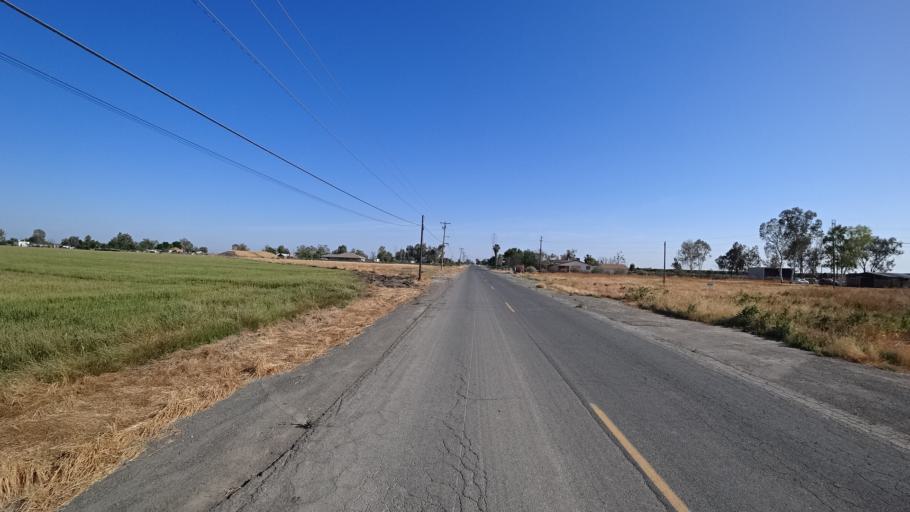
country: US
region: California
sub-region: Kings County
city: Corcoran
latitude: 36.1172
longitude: -119.5633
